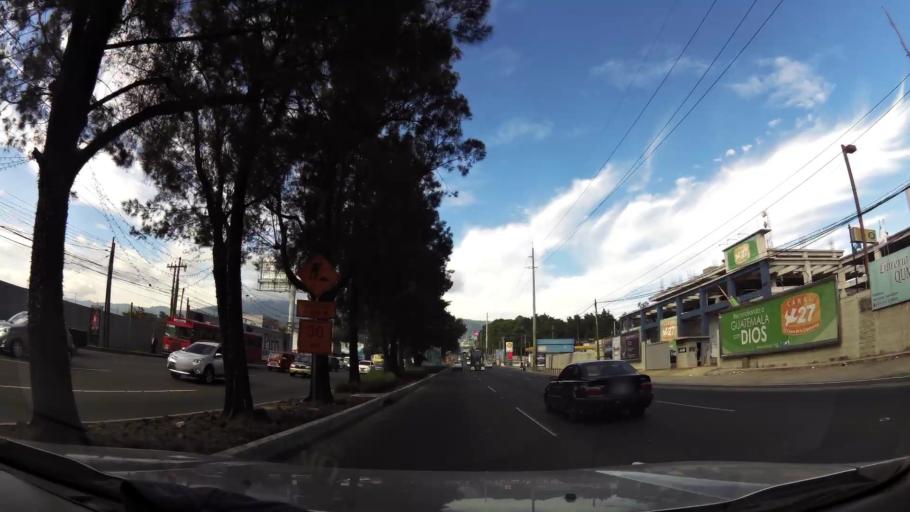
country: GT
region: Guatemala
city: Mixco
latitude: 14.6347
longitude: -90.5887
